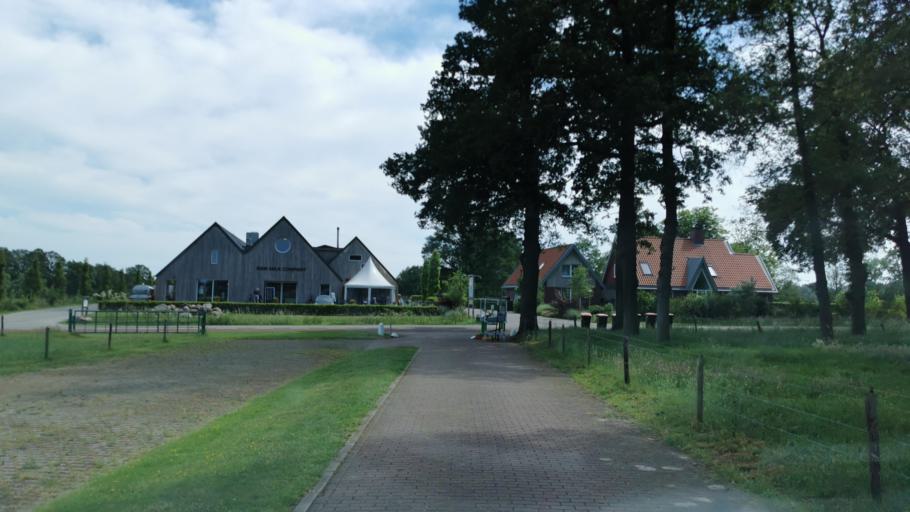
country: NL
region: Overijssel
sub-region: Gemeente Losser
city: Losser
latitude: 52.3224
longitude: 7.0052
